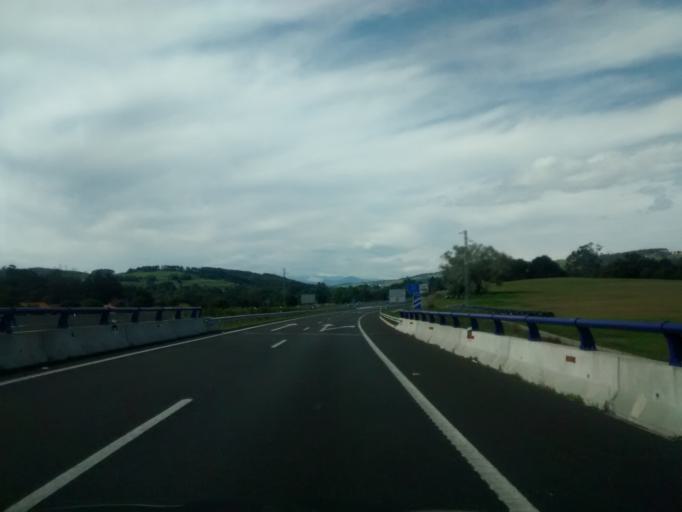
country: ES
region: Cantabria
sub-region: Provincia de Cantabria
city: El Astillero
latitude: 43.3855
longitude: -3.8452
